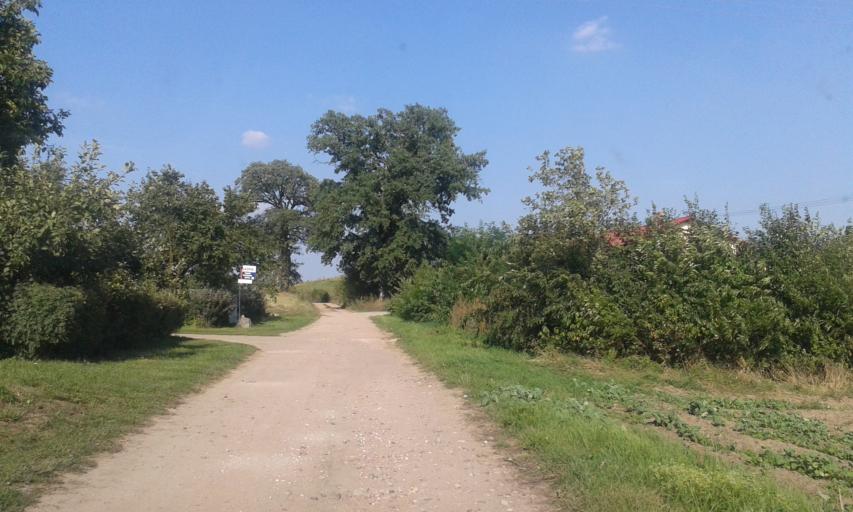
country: PL
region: Kujawsko-Pomorskie
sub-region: Powiat swiecki
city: Nowe
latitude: 53.6790
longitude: 18.7358
